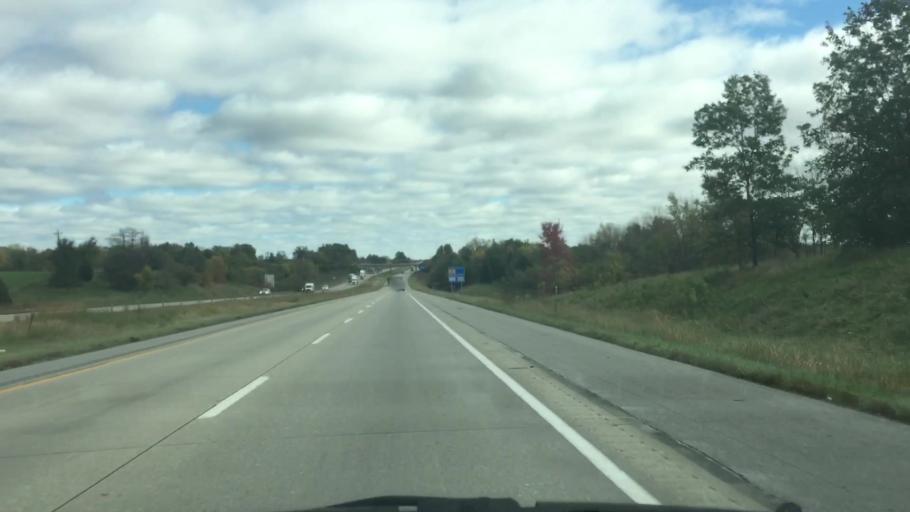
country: US
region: Iowa
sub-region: Jasper County
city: Newton
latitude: 41.6834
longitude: -93.0566
